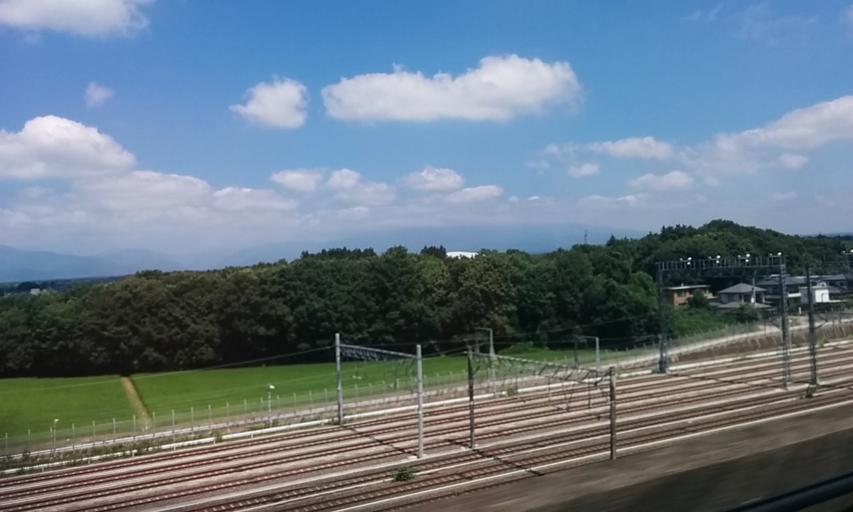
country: JP
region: Tochigi
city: Kuroiso
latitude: 36.9451
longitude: 140.0351
